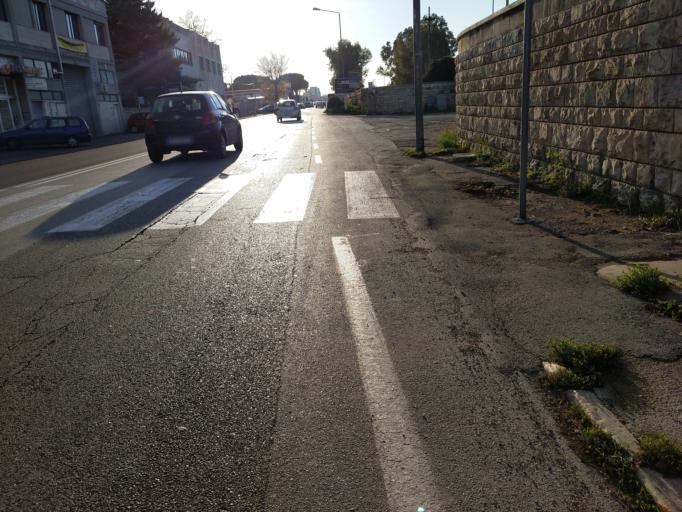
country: IT
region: Apulia
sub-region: Provincia di Bari
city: Bari
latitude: 41.1125
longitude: 16.8301
